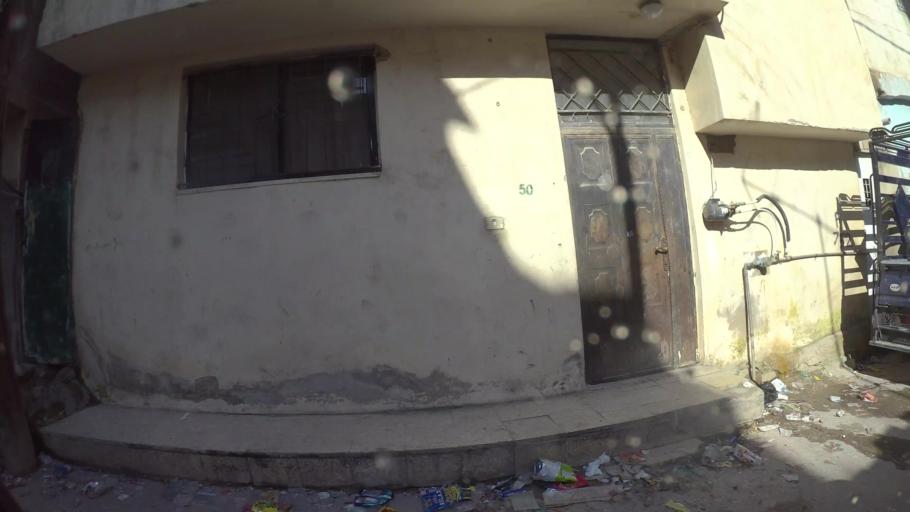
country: JO
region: Amman
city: Al Jubayhah
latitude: 32.0733
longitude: 35.8412
